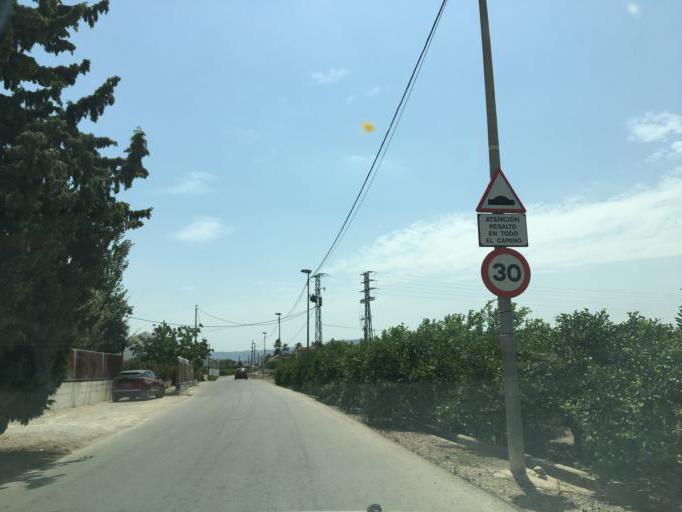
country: ES
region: Murcia
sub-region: Murcia
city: Santomera
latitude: 38.0359
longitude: -1.0544
